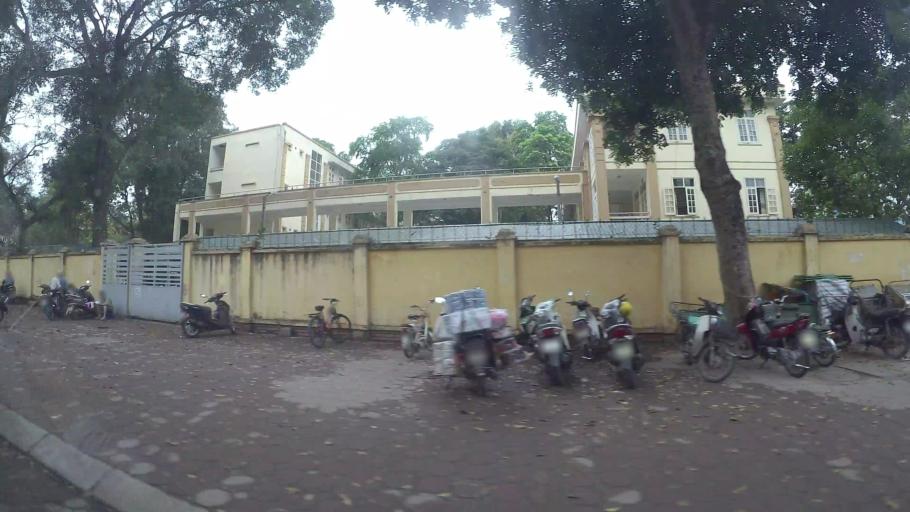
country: VN
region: Ha Noi
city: Hai BaTrung
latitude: 21.0058
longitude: 105.8353
